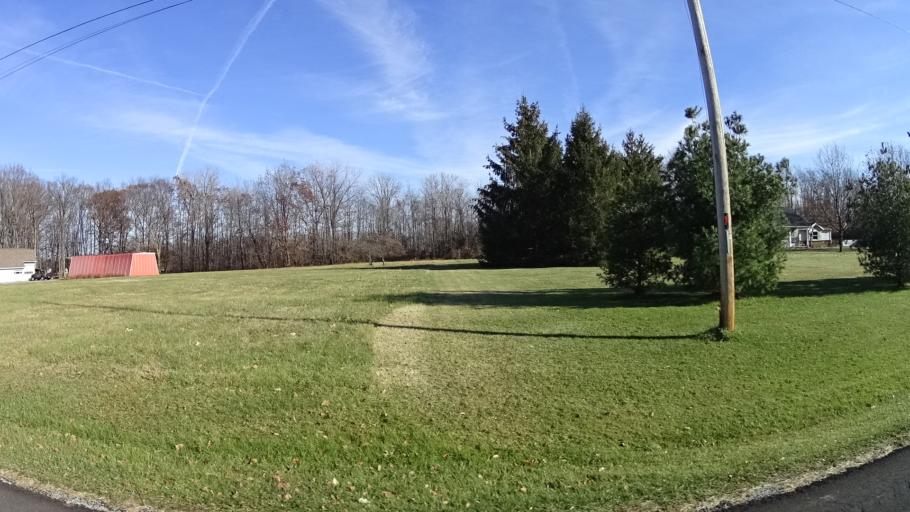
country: US
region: Ohio
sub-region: Lorain County
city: Wellington
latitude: 41.1167
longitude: -82.2390
